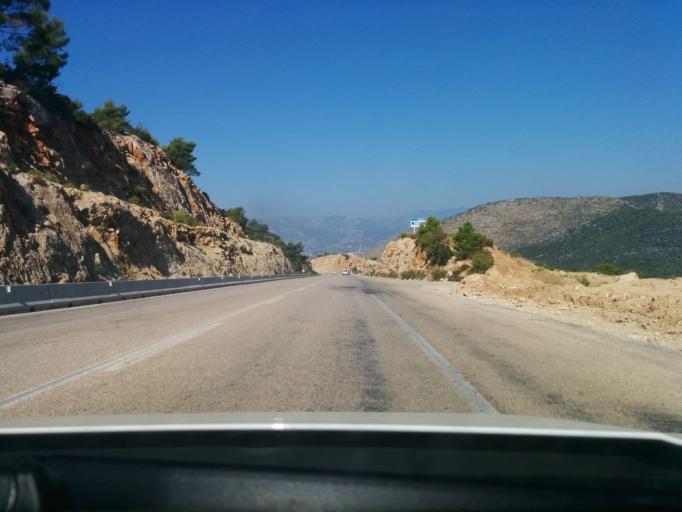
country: TR
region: Antalya
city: Kalkan
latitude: 36.2765
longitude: 29.3920
